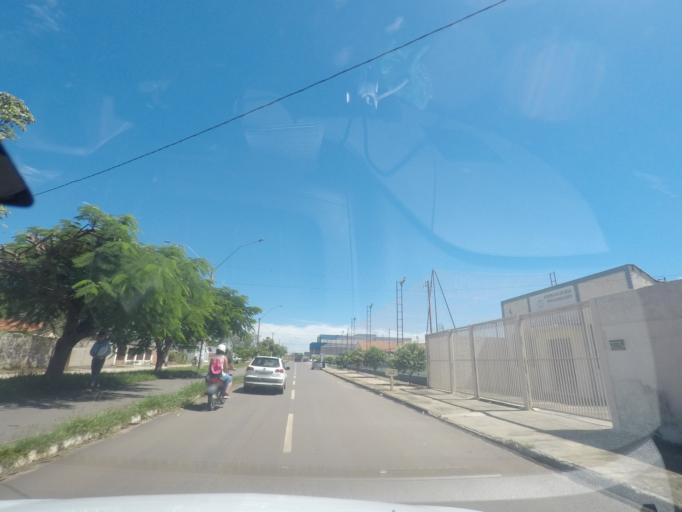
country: BR
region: Goias
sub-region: Aparecida De Goiania
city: Aparecida de Goiania
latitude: -16.7774
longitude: -49.3364
